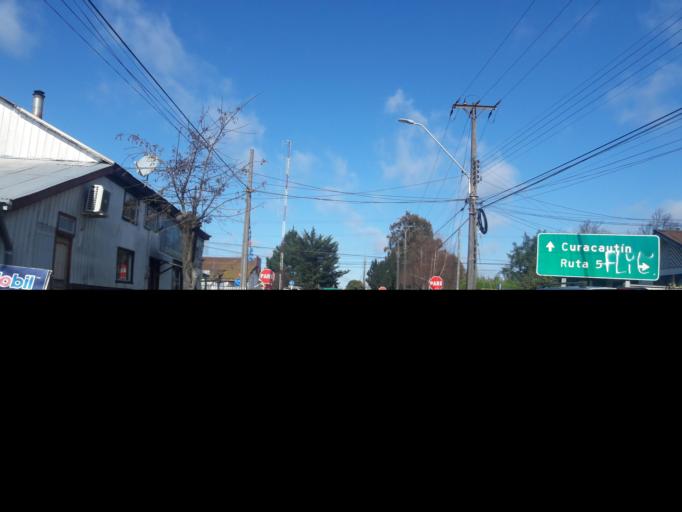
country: CL
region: Araucania
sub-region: Provincia de Malleco
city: Victoria
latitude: -38.2394
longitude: -72.3294
